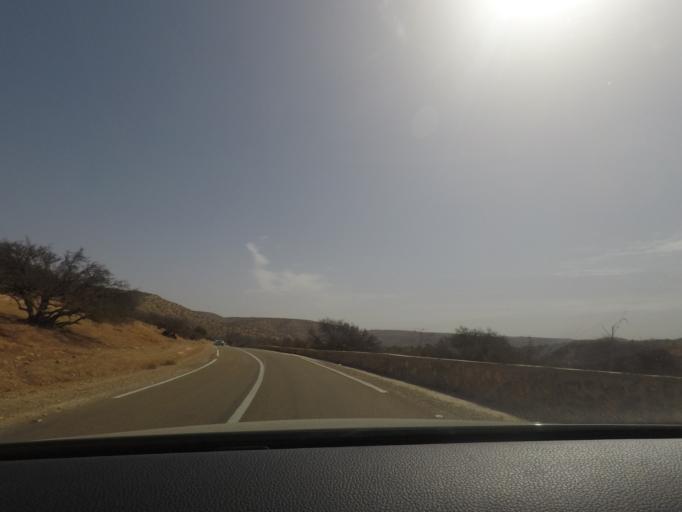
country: MA
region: Marrakech-Tensift-Al Haouz
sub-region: Essaouira
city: Tamanar
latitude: 31.0870
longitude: -9.6762
